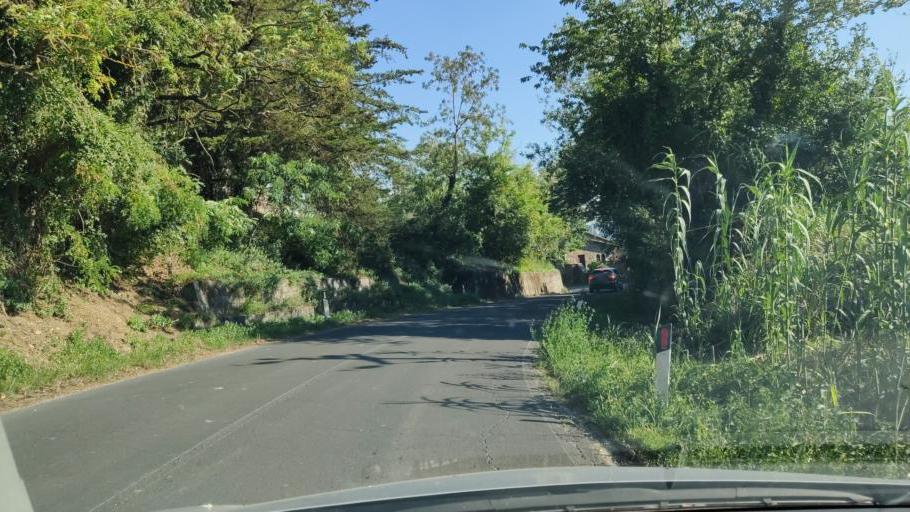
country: IT
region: Umbria
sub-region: Provincia di Terni
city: Penna in Teverina
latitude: 42.4896
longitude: 12.3538
